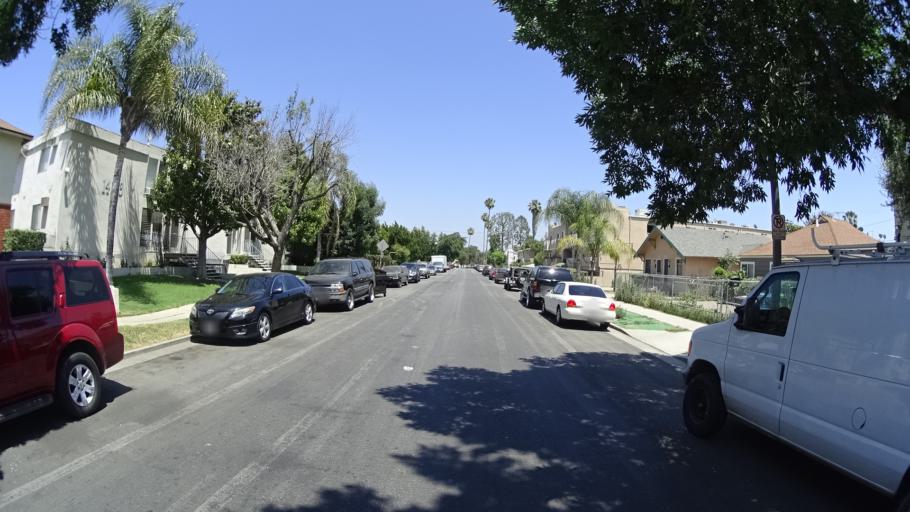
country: US
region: California
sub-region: Los Angeles County
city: Van Nuys
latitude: 34.1877
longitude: -118.4417
